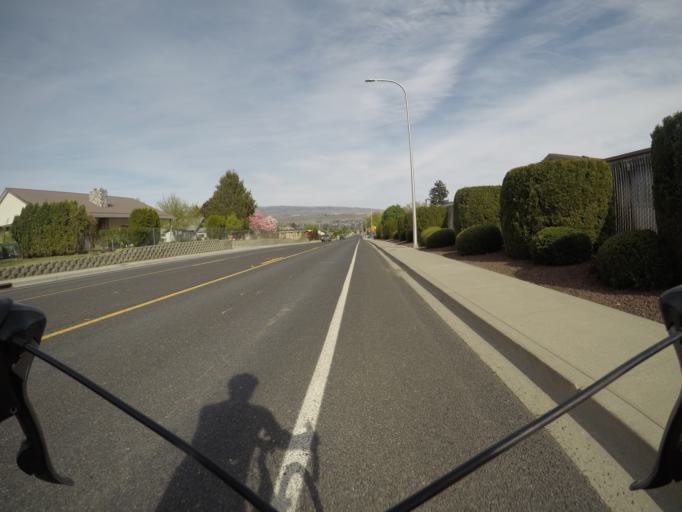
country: US
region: Washington
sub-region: Chelan County
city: West Wenatchee
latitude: 47.4424
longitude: -120.3421
